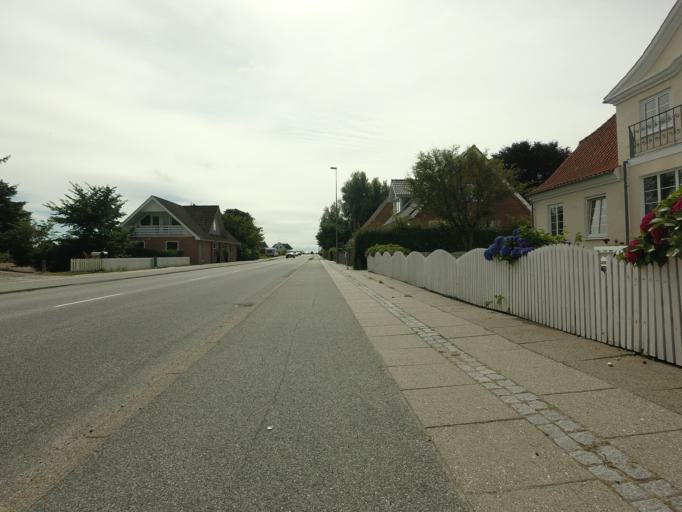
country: DK
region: North Denmark
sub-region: Hjorring Kommune
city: Vra
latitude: 57.3938
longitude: 9.7814
